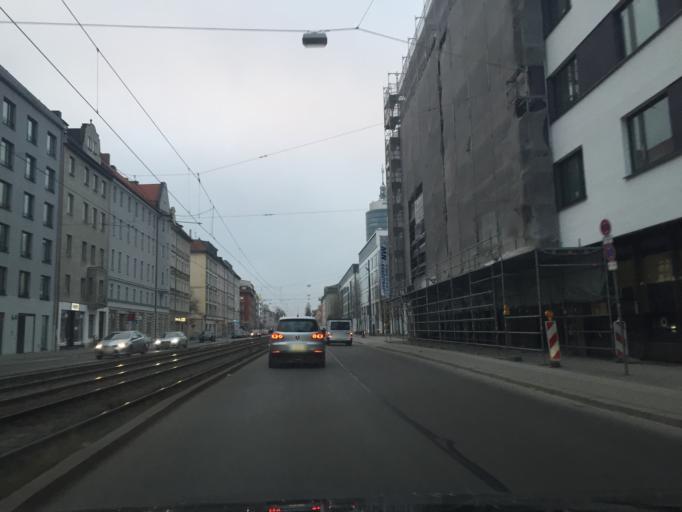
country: DE
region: Bavaria
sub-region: Upper Bavaria
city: Munich
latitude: 48.1397
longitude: 11.5407
